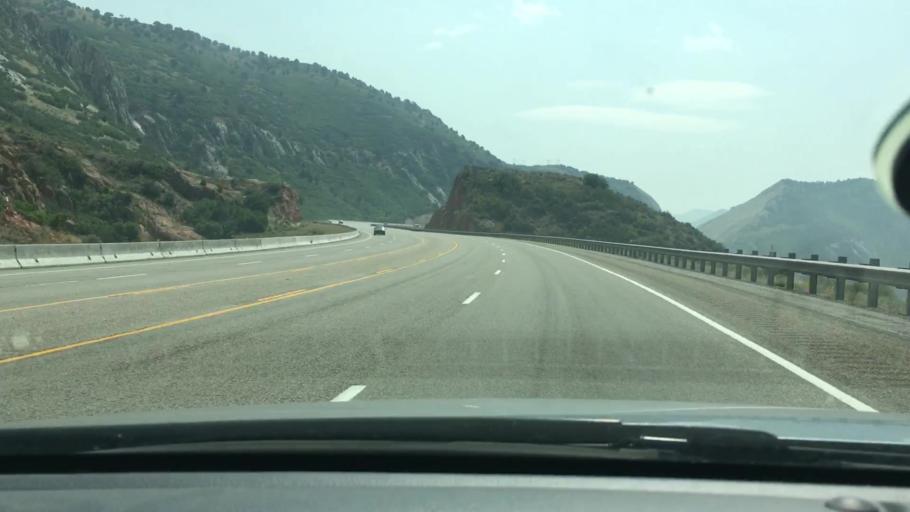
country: US
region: Utah
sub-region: Utah County
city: Mapleton
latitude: 40.0185
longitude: -111.4962
